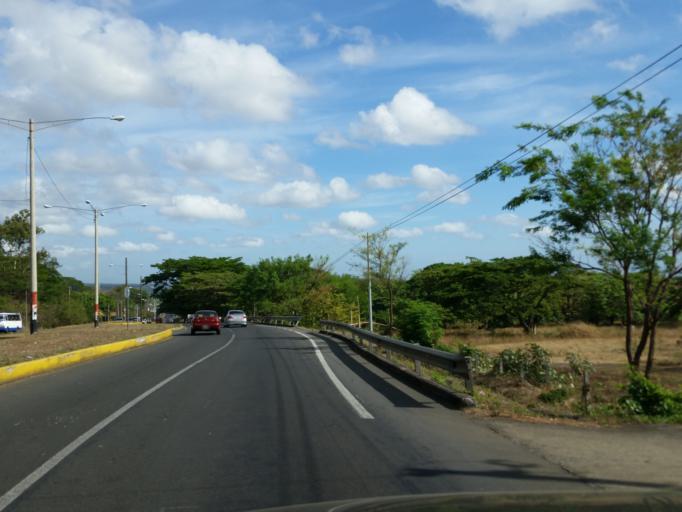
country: NI
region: Masaya
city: Ticuantepe
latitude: 12.0288
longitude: -86.1785
